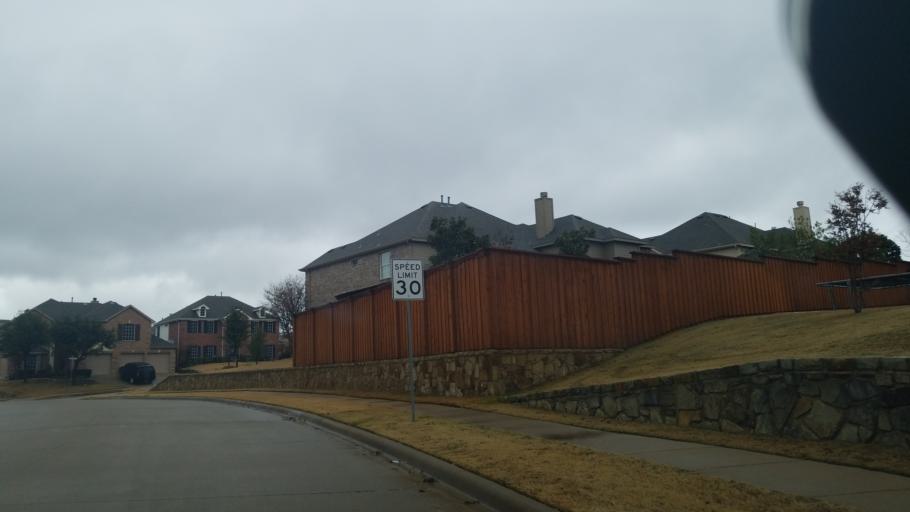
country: US
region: Texas
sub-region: Denton County
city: Corinth
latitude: 33.1396
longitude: -97.0914
